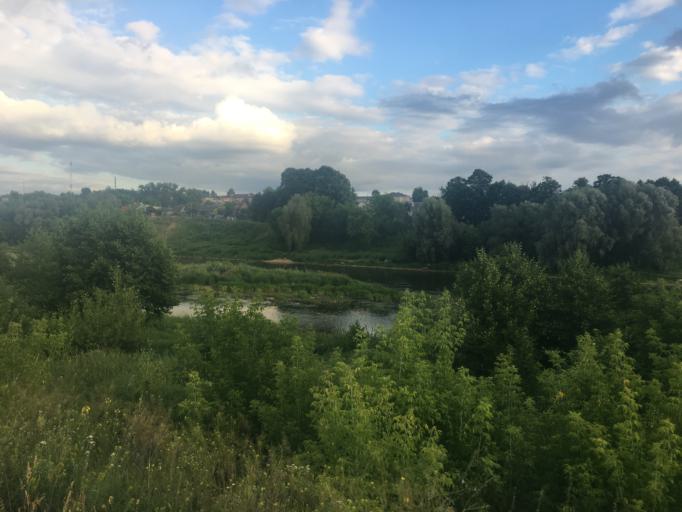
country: BY
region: Grodnenskaya
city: Hrodna
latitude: 53.6795
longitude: 23.8084
